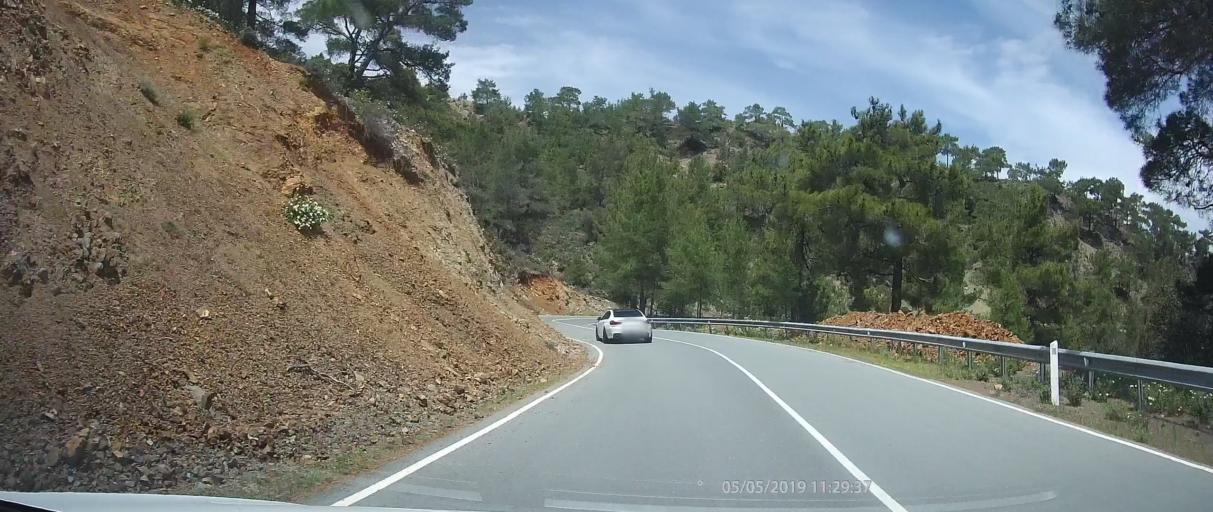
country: CY
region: Limassol
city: Pachna
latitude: 34.9416
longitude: 32.6490
